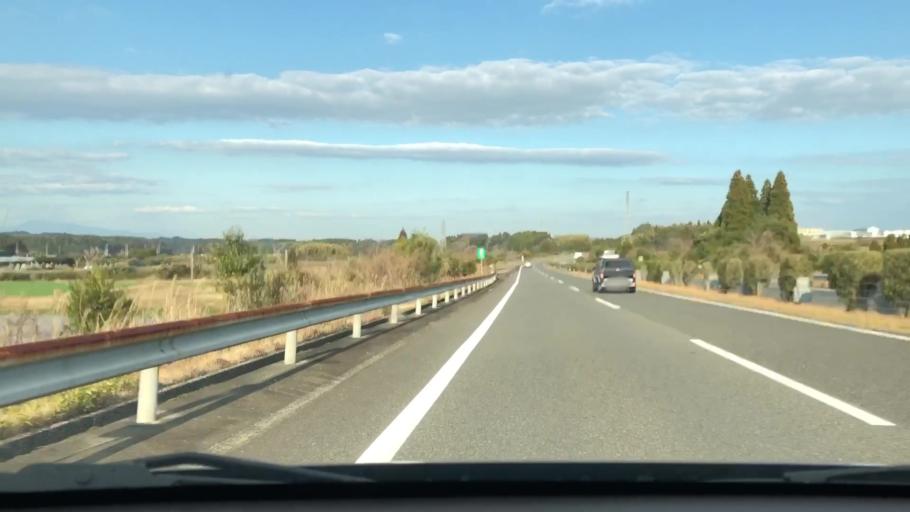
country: JP
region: Miyazaki
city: Miyazaki-shi
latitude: 31.8254
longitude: 131.3087
